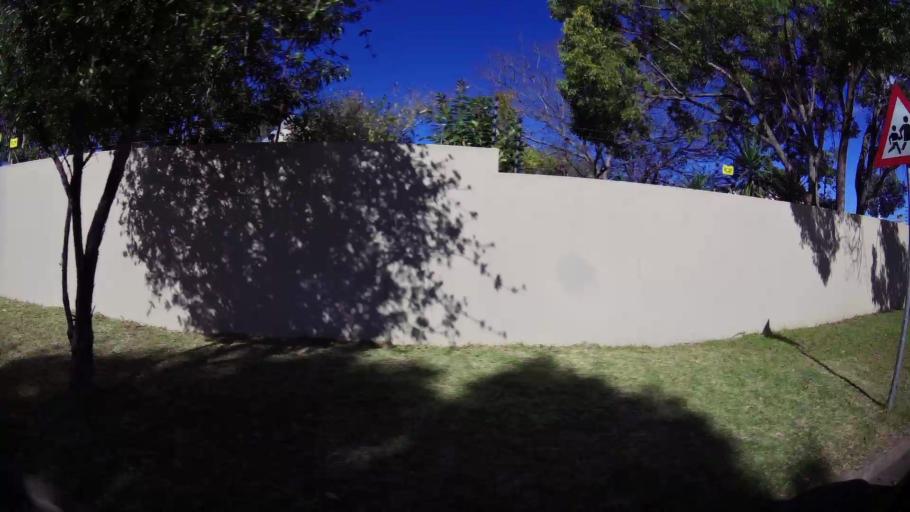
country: ZA
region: Western Cape
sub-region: Eden District Municipality
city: George
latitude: -33.9580
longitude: 22.4325
